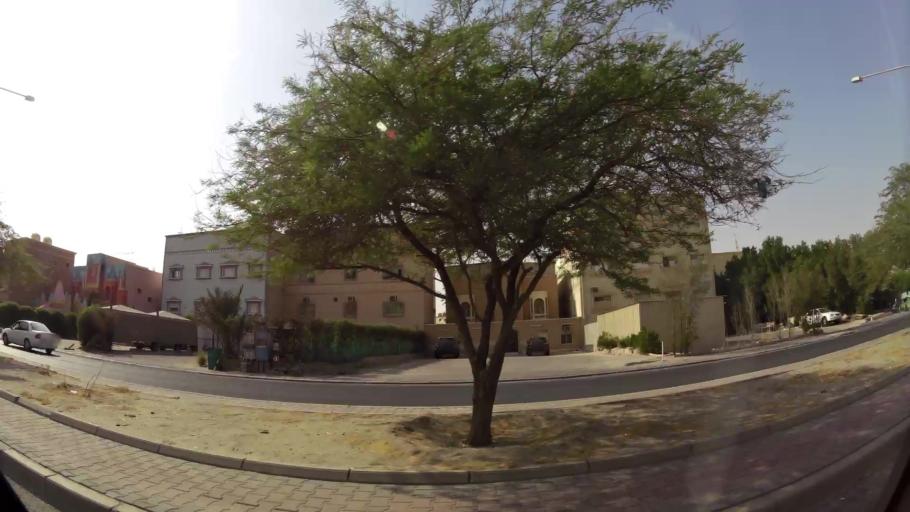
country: KW
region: Muhafazat al Jahra'
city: Al Jahra'
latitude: 29.3175
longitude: 47.6781
